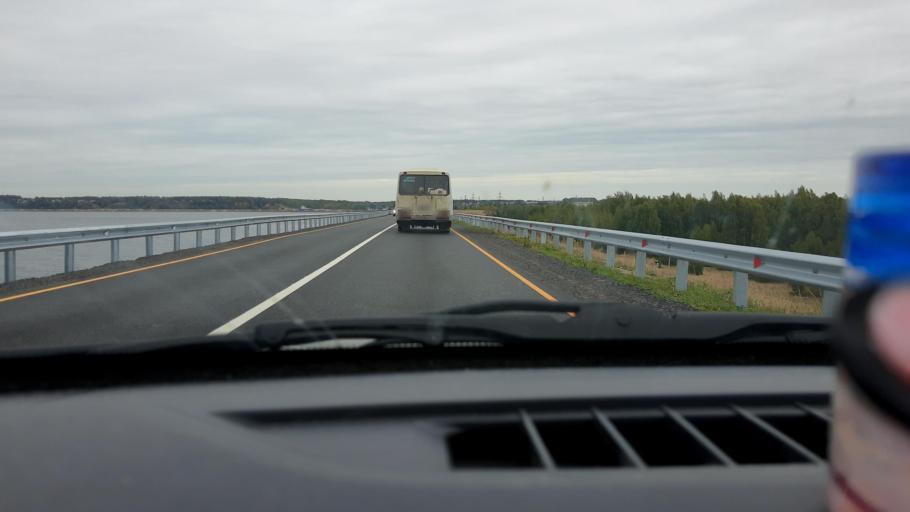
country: RU
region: Nizjnij Novgorod
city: Zavolzh'ye
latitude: 56.6698
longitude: 43.3990
